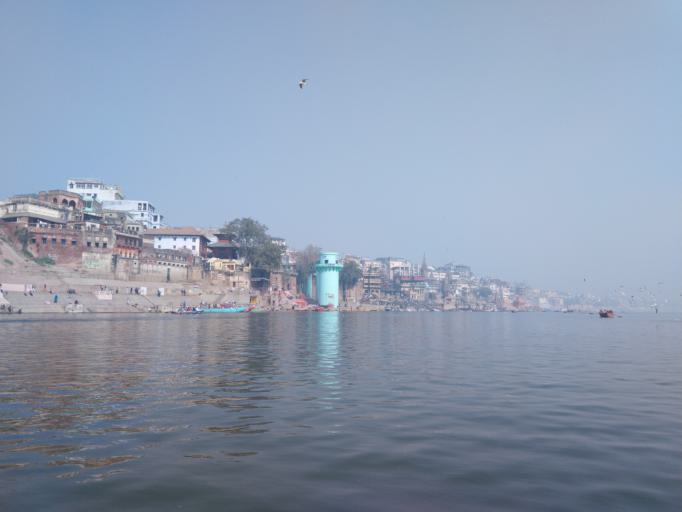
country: IN
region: Uttar Pradesh
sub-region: Varanasi
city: Varanasi
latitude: 25.3083
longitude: 83.0131
